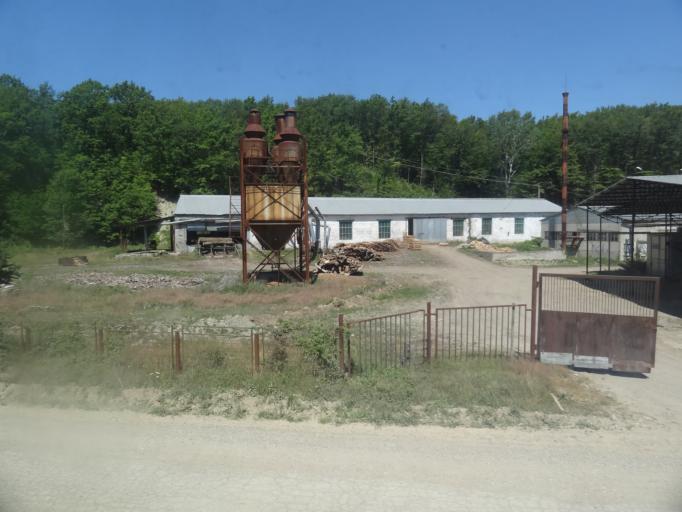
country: RU
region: Krasnodarskiy
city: Goryachiy Klyuch
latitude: 44.6341
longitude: 39.0983
